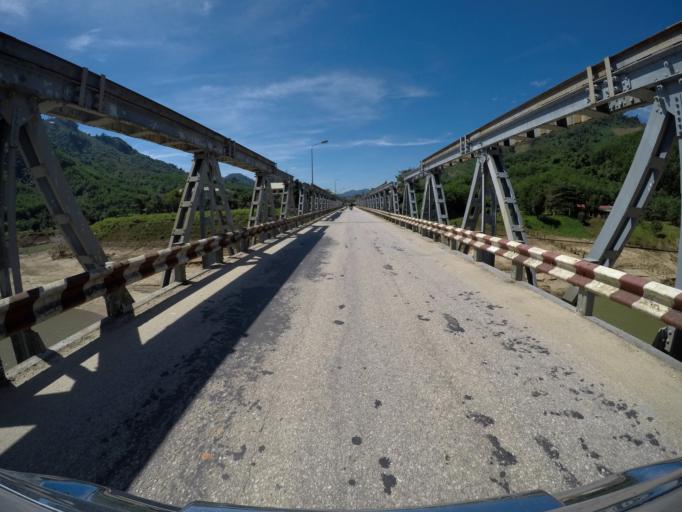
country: VN
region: Quang Nam
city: Thanh My
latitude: 15.6917
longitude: 107.7684
